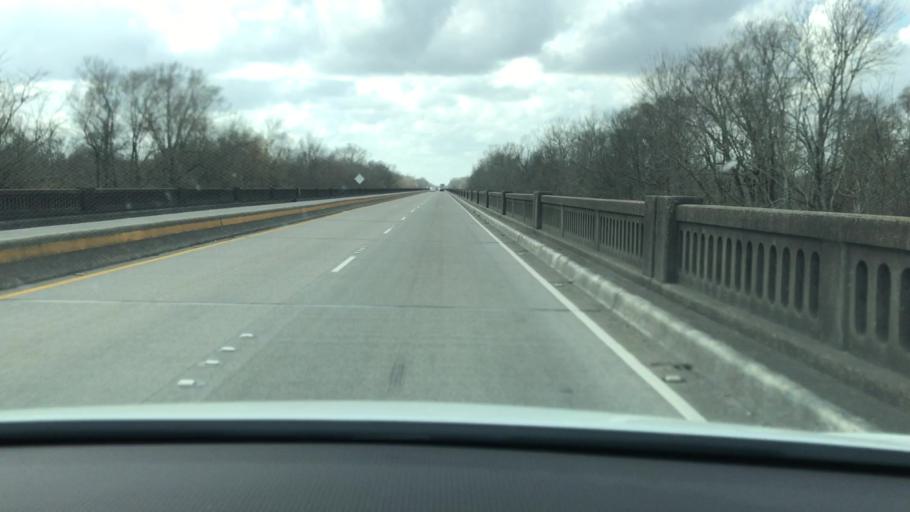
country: US
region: Louisiana
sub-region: Saint Landry Parish
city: Krotz Springs
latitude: 30.5551
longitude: -91.6829
